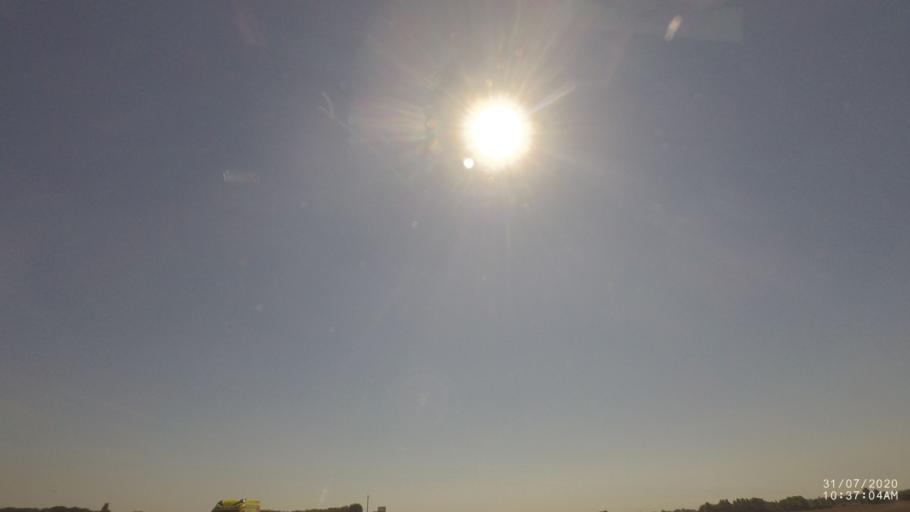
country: SK
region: Trnavsky
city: Dunajska Streda
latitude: 48.0096
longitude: 17.4664
